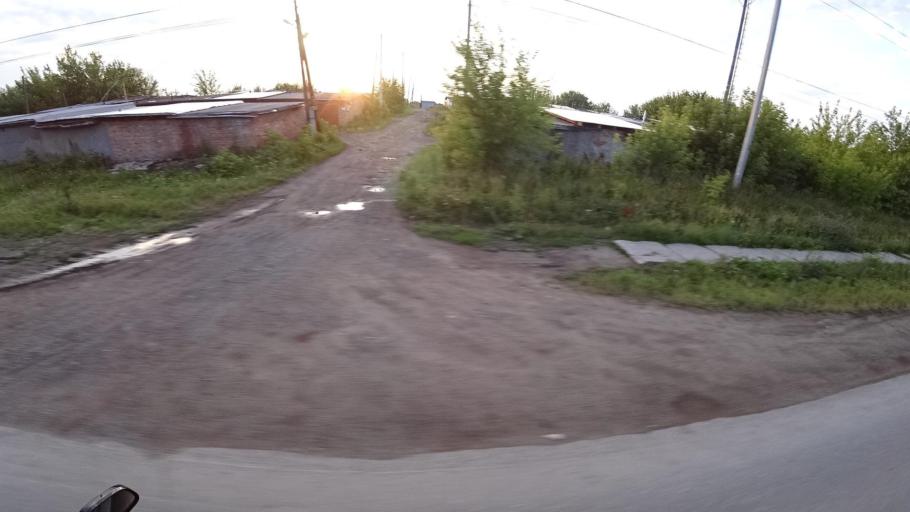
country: RU
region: Sverdlovsk
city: Kamyshlov
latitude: 56.8556
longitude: 62.7206
